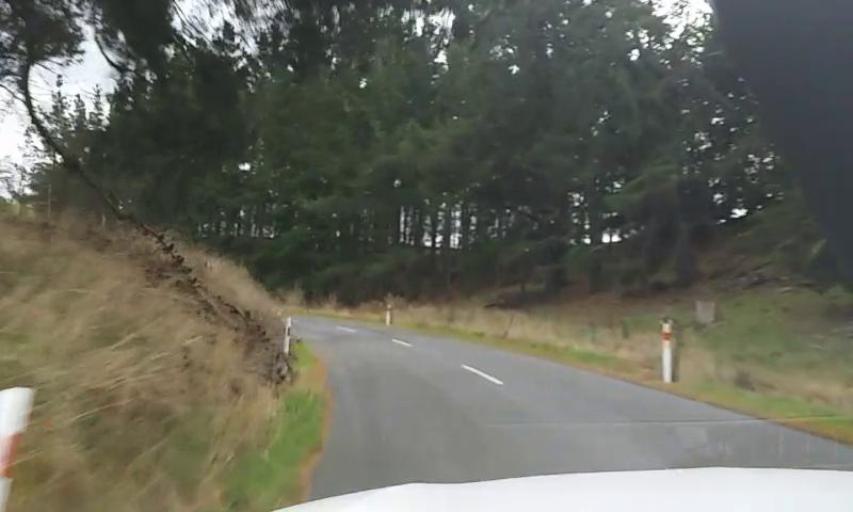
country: NZ
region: Canterbury
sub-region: Waimakariri District
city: Kaiapoi
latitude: -43.2979
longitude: 172.4383
